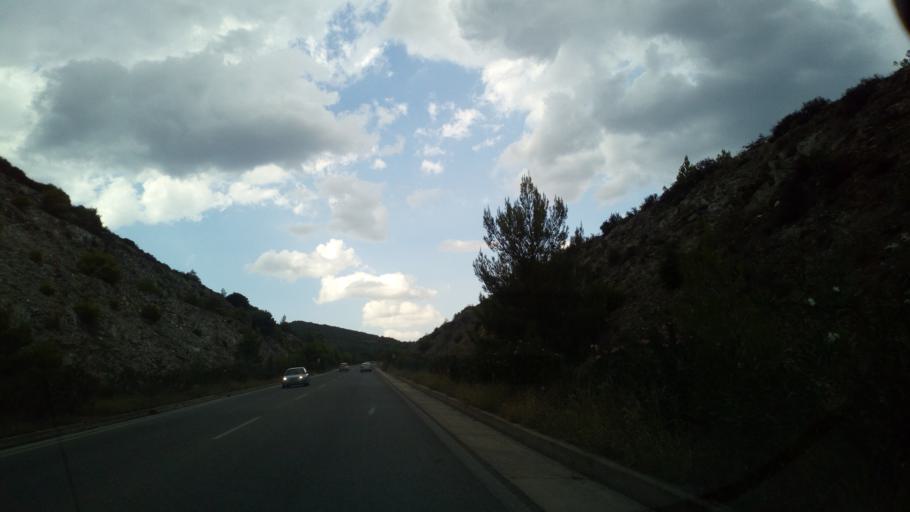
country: GR
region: Central Macedonia
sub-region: Nomos Chalkidikis
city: Polygyros
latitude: 40.3450
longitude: 23.4509
